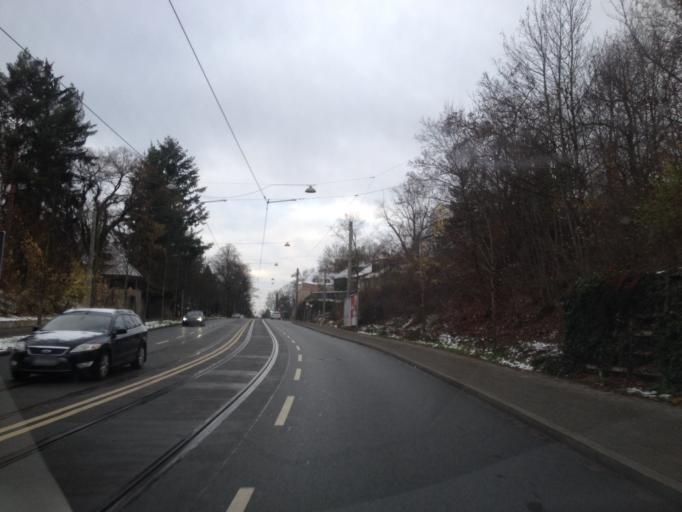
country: DE
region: Bavaria
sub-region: Regierungsbezirk Mittelfranken
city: Nuernberg
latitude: 49.4711
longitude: 11.1332
